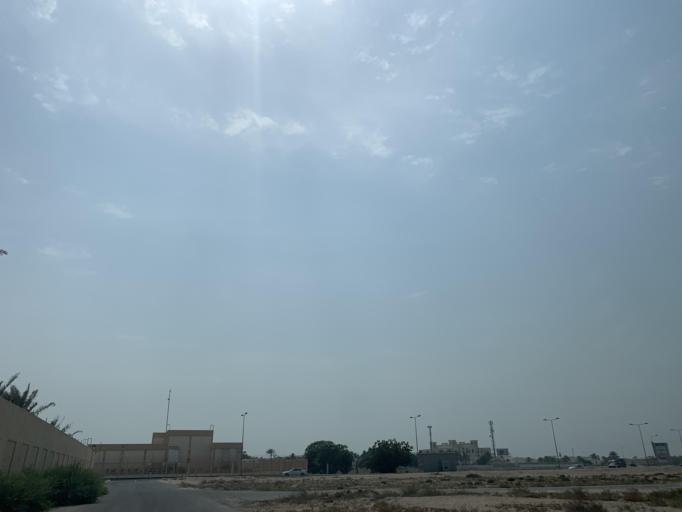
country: BH
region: Manama
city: Jidd Hafs
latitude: 26.2144
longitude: 50.4812
